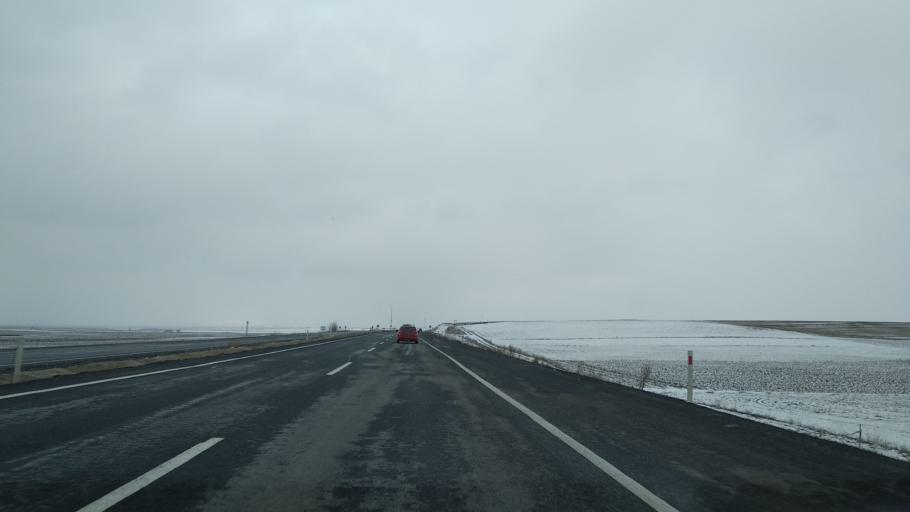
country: TR
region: Kayseri
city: Elbasi
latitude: 38.6468
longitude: 35.9637
